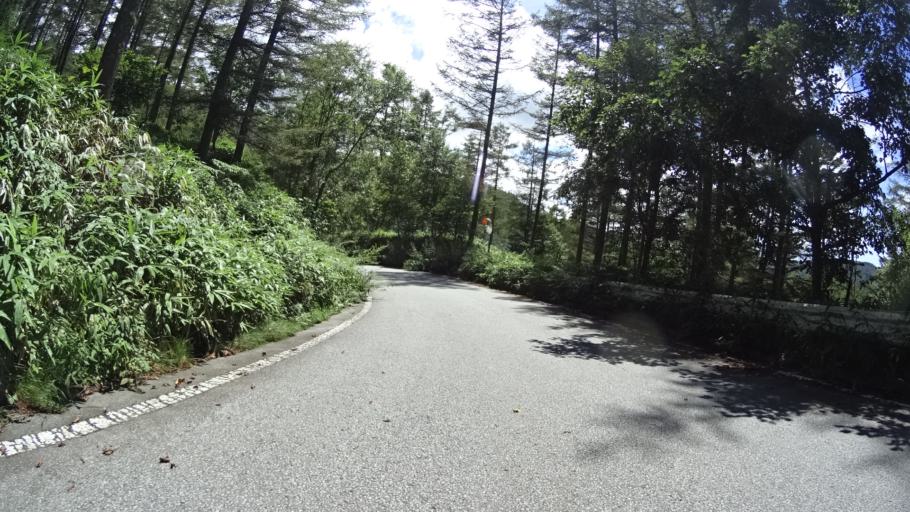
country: JP
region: Yamanashi
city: Enzan
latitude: 35.7266
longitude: 138.8426
